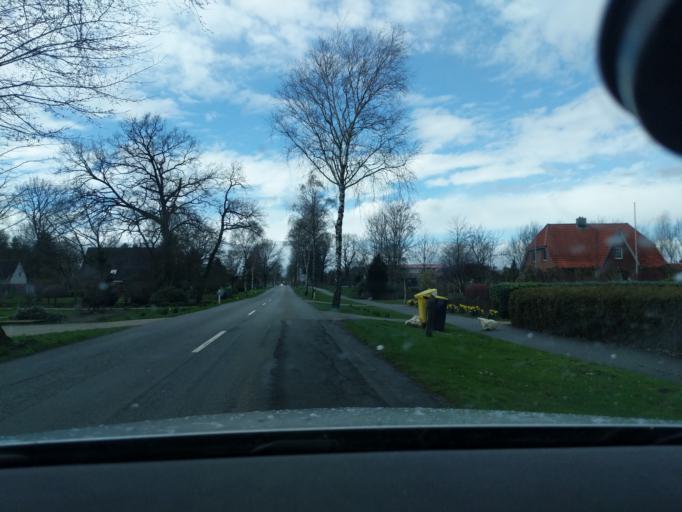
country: DE
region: Lower Saxony
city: Drochtersen
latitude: 53.6665
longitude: 9.3910
